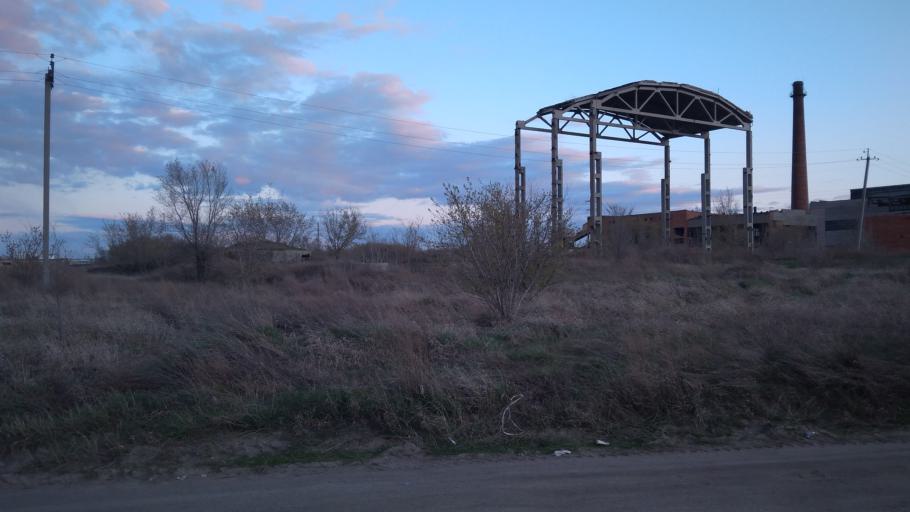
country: RU
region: Chelyabinsk
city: Troitsk
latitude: 54.0699
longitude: 61.5770
